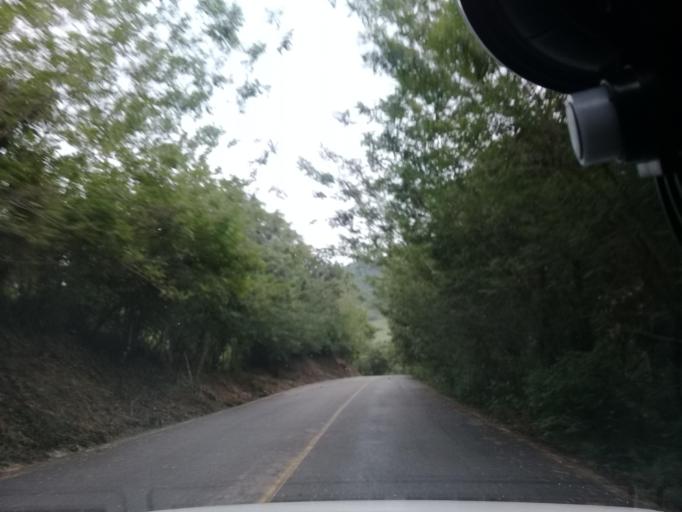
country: MX
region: Veracruz
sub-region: Chalma
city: San Pedro Coyutla
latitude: 21.2102
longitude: -98.4230
